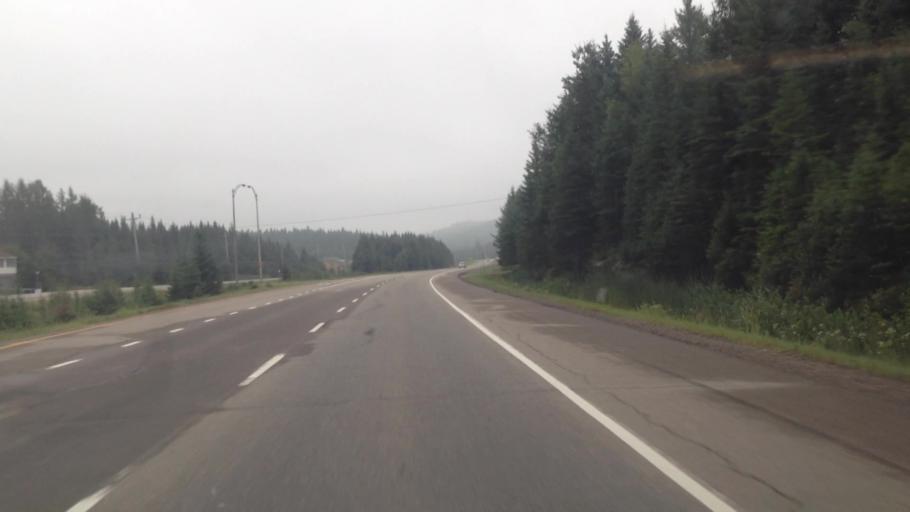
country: CA
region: Quebec
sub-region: Laurentides
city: Sainte-Agathe-des-Monts
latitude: 46.1024
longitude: -74.3831
